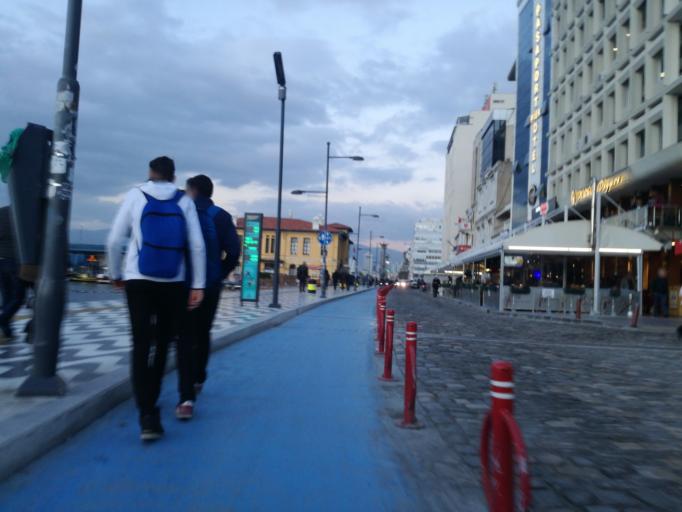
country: TR
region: Izmir
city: Izmir
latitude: 38.4277
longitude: 27.1324
